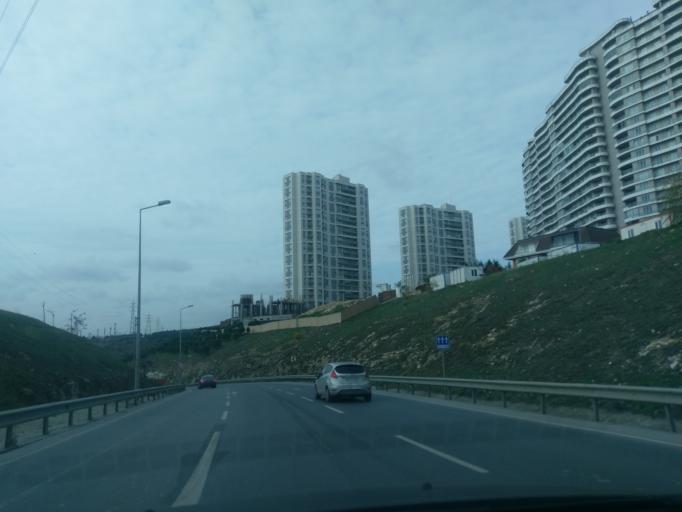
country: TR
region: Istanbul
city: Basaksehir
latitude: 41.0633
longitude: 28.7778
